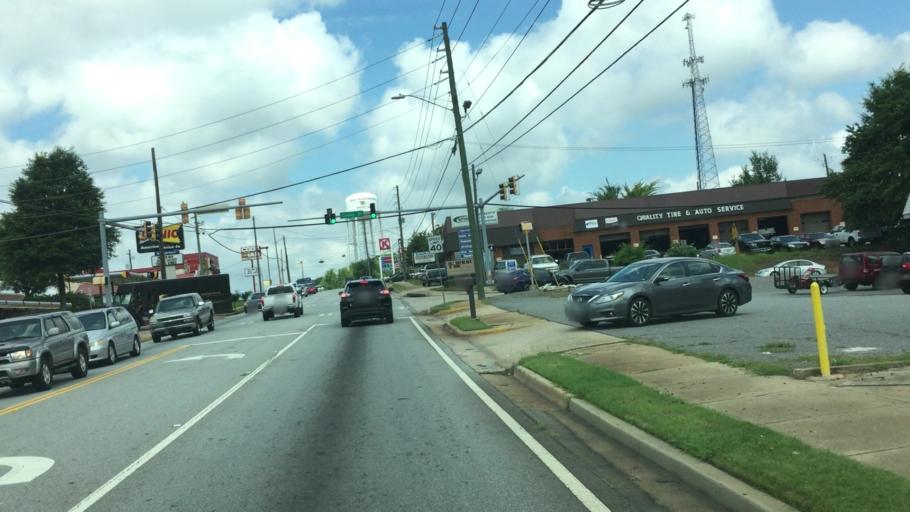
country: US
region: Georgia
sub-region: Barrow County
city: Winder
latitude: 33.9915
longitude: -83.7242
